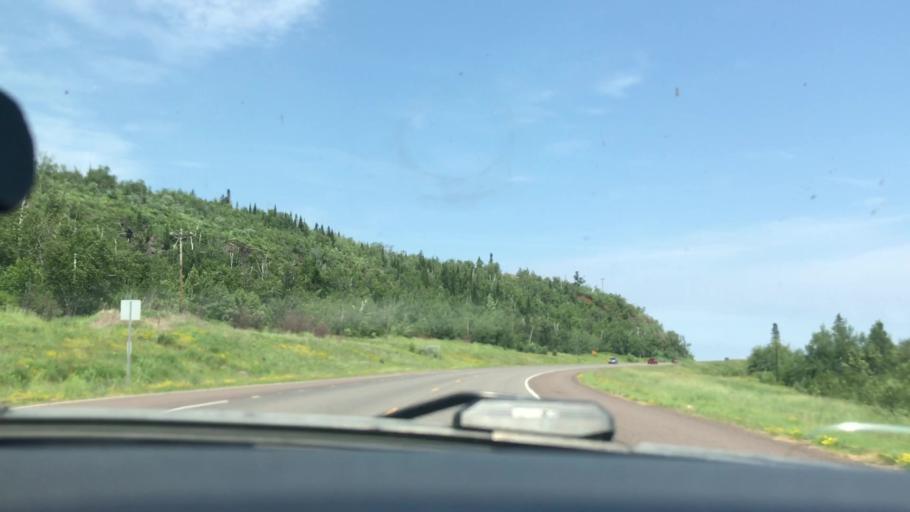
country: US
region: Minnesota
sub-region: Lake County
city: Silver Bay
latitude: 47.3025
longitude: -91.2503
